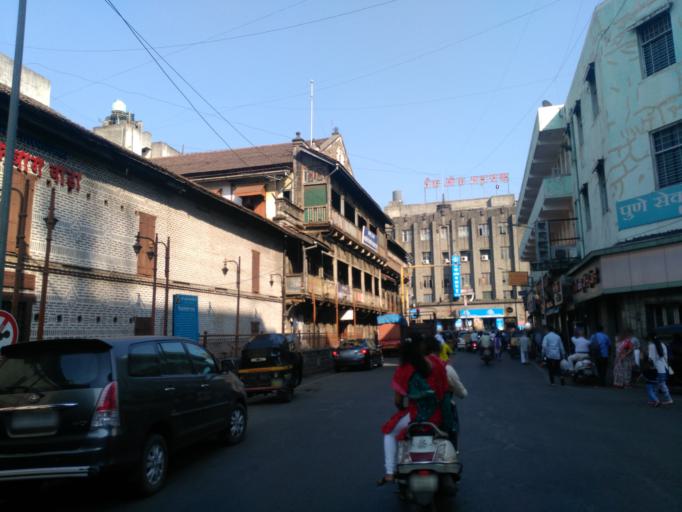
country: IN
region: Maharashtra
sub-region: Pune Division
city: Pune
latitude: 18.5137
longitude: 73.8530
